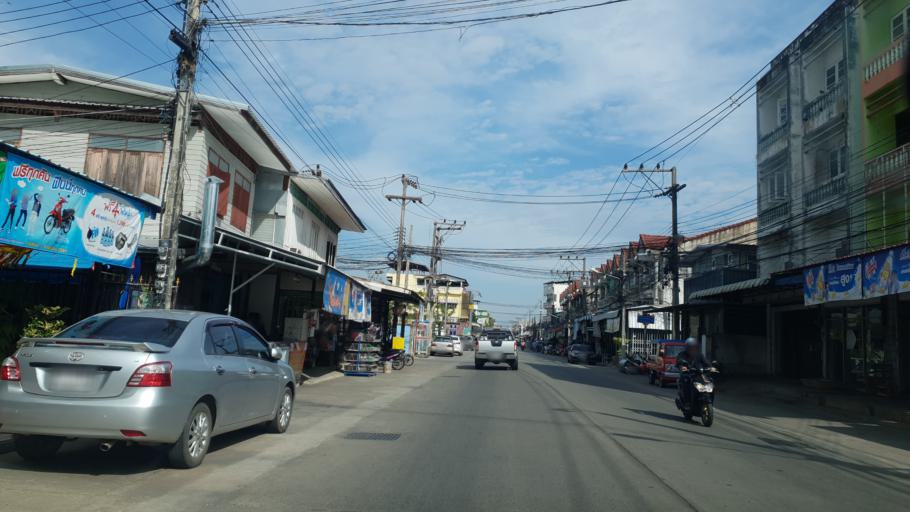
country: TH
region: Phitsanulok
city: Phitsanulok
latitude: 16.8078
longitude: 100.2676
